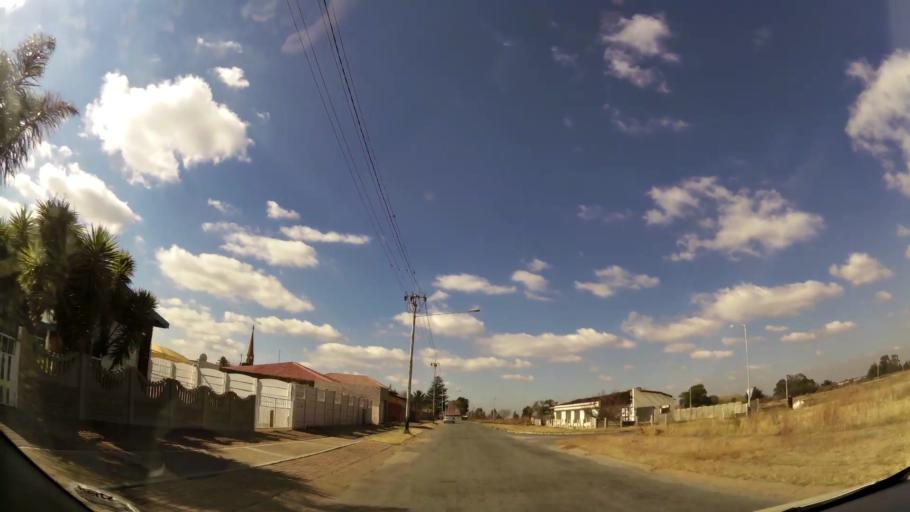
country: ZA
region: Gauteng
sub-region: West Rand District Municipality
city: Krugersdorp
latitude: -26.1226
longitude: 27.8064
